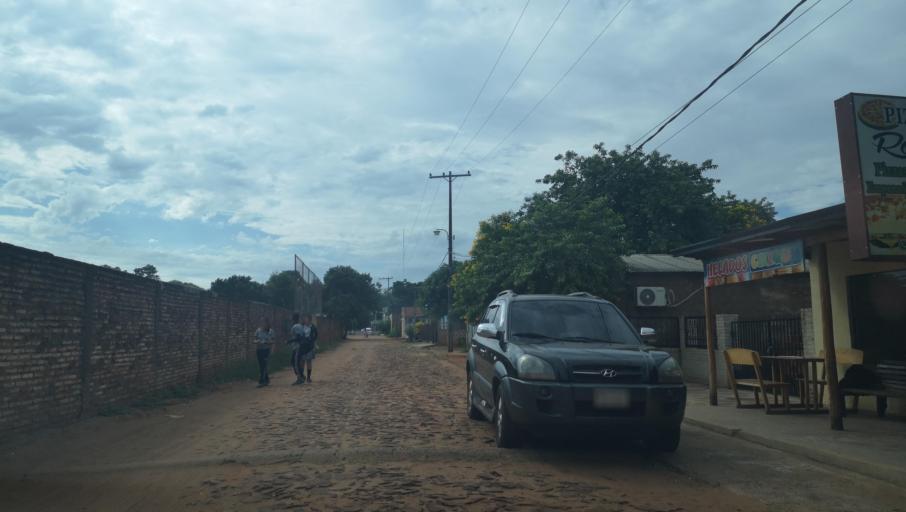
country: PY
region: San Pedro
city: Capiibary
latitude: -24.7280
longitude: -56.0207
